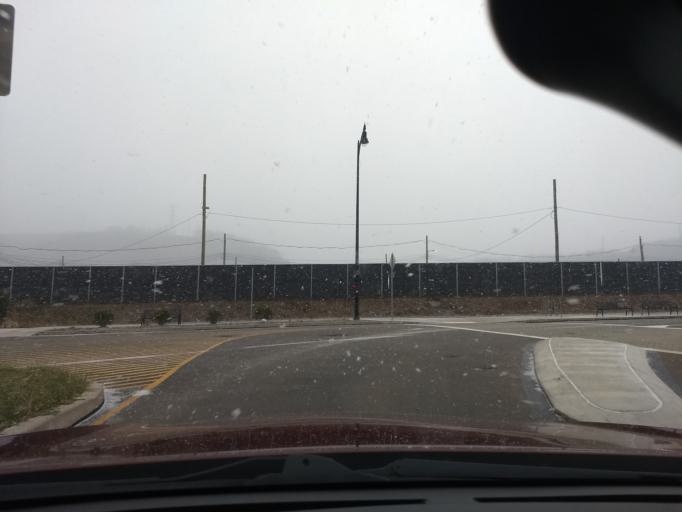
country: US
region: Pennsylvania
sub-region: Allegheny County
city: Homestead
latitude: 40.4107
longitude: -79.9478
